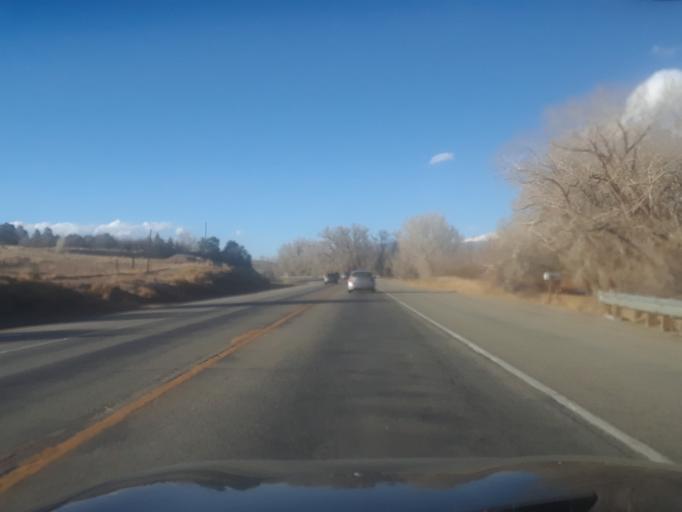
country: US
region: Colorado
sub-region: Chaffee County
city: Buena Vista
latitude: 38.7757
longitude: -106.1064
